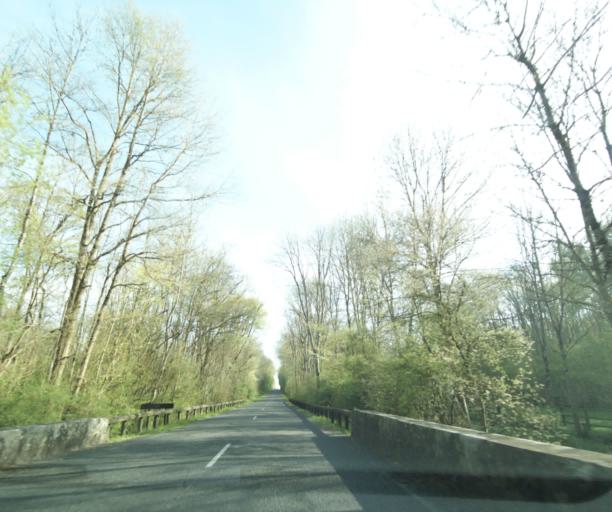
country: FR
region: Ile-de-France
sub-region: Departement de Seine-et-Marne
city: Nangis
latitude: 48.5326
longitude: 2.9823
